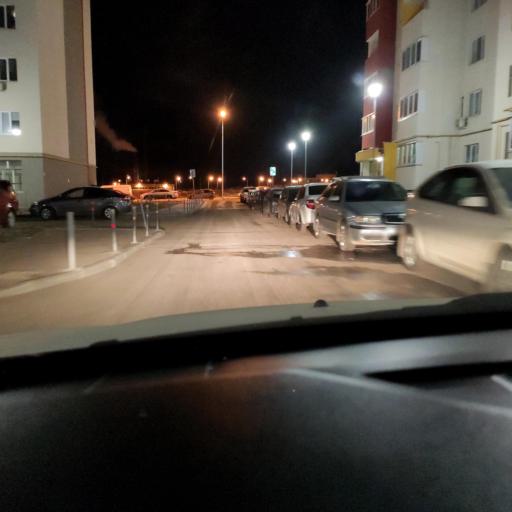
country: RU
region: Samara
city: Samara
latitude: 53.0950
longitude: 50.1673
